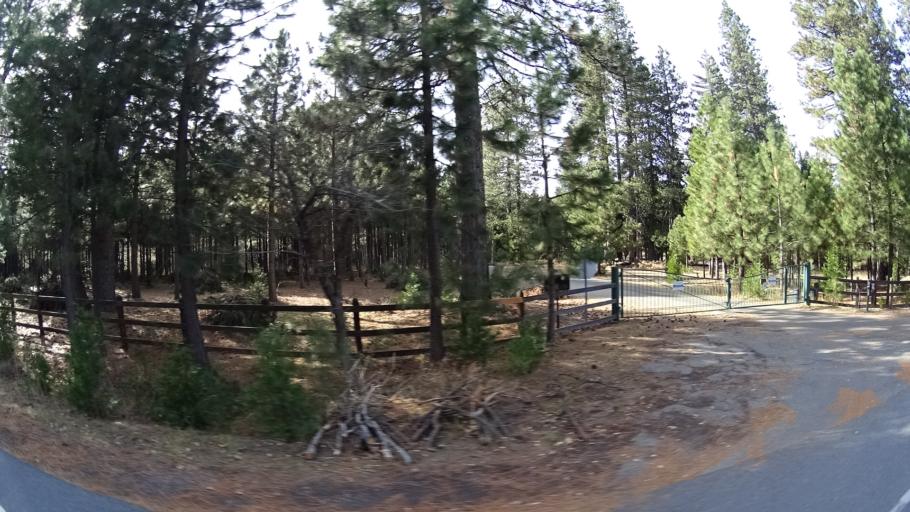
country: US
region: California
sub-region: Siskiyou County
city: Weed
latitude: 41.3879
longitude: -122.4096
